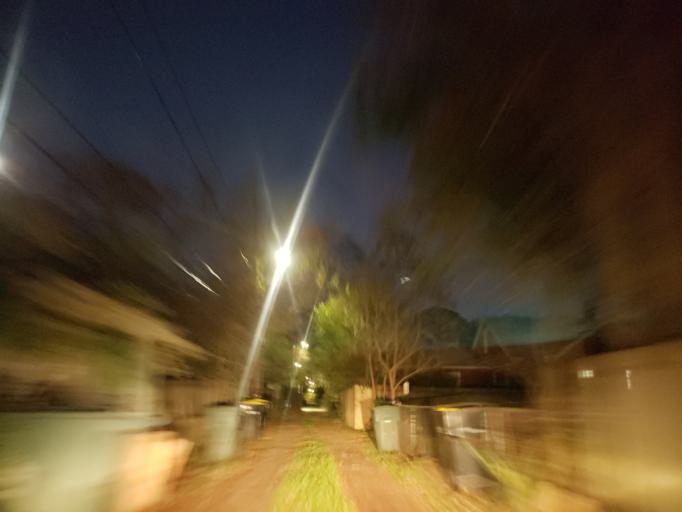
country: US
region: Georgia
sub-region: Chatham County
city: Savannah
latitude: 32.0430
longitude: -81.0924
